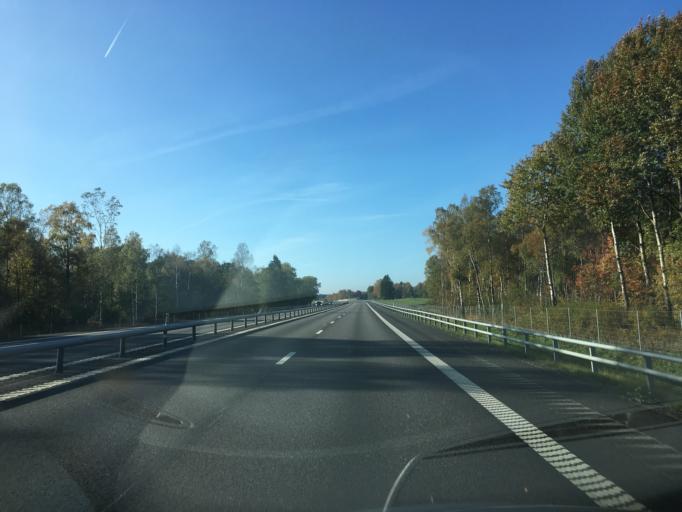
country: SE
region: Skane
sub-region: Horby Kommun
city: Hoerby
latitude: 55.9257
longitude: 13.8210
